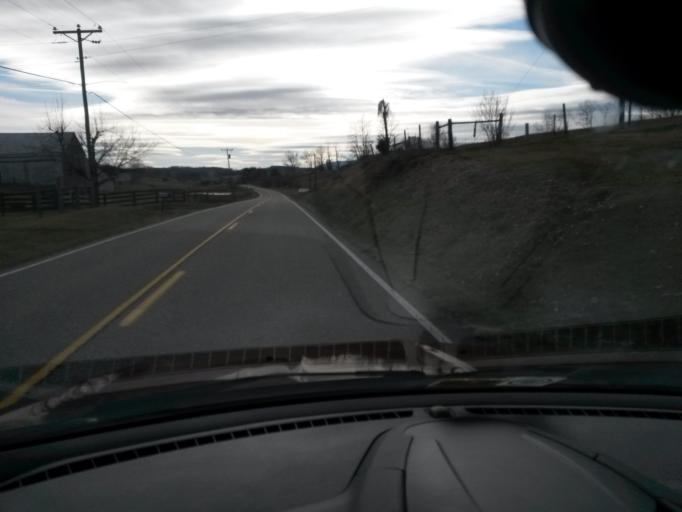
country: US
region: Virginia
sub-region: City of Staunton
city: Staunton
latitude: 38.2517
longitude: -79.1632
